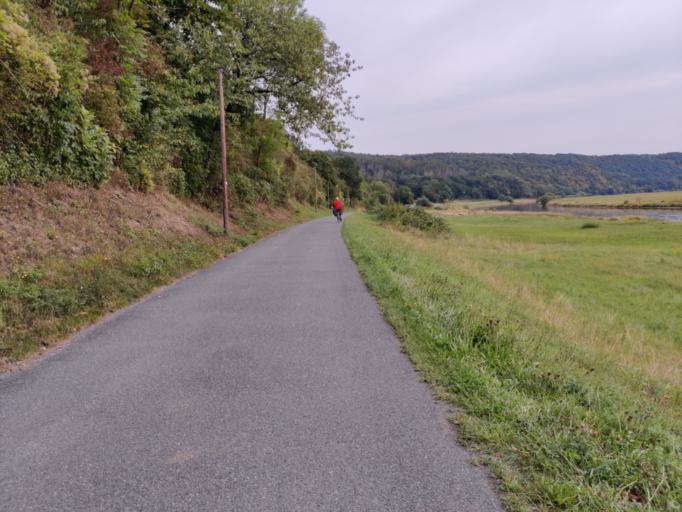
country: DE
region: Lower Saxony
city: Hehlen
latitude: 51.9929
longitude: 9.4775
